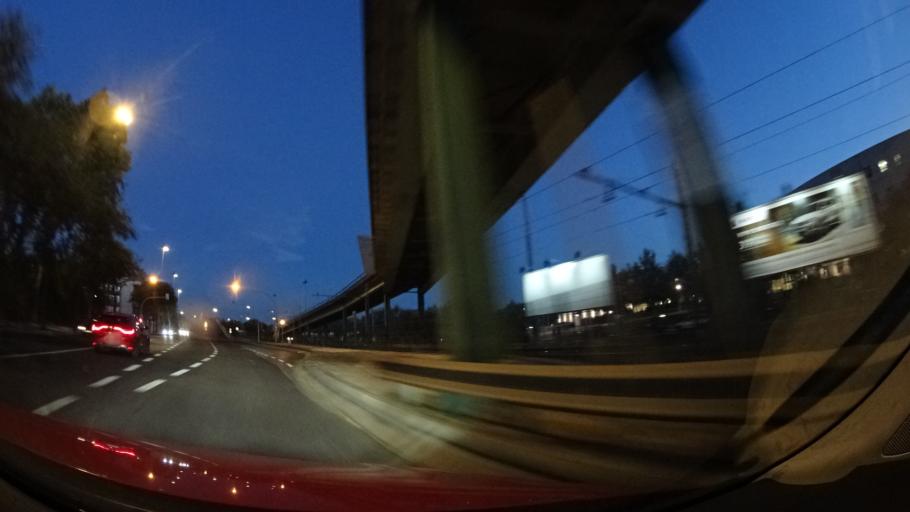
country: PT
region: Lisbon
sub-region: Oeiras
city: Alges
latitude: 38.6945
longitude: -9.2210
